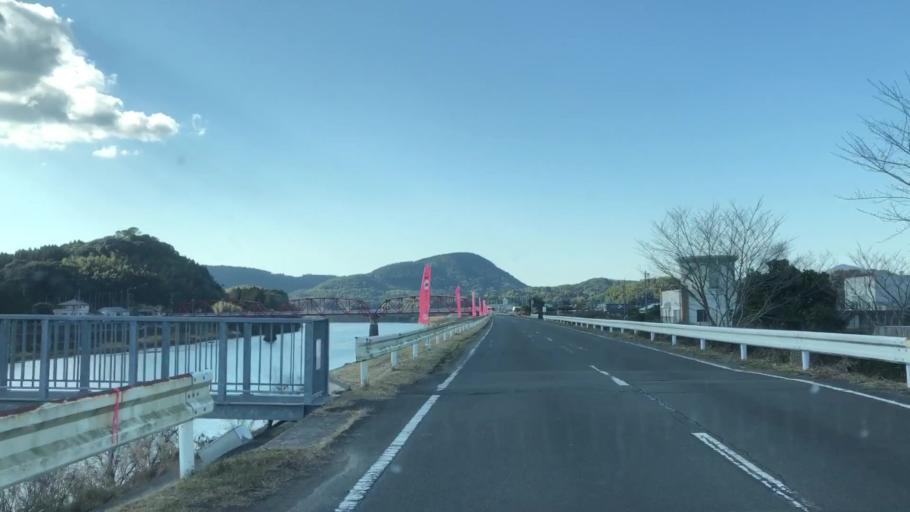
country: JP
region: Kagoshima
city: Satsumasendai
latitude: 31.8612
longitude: 130.3409
